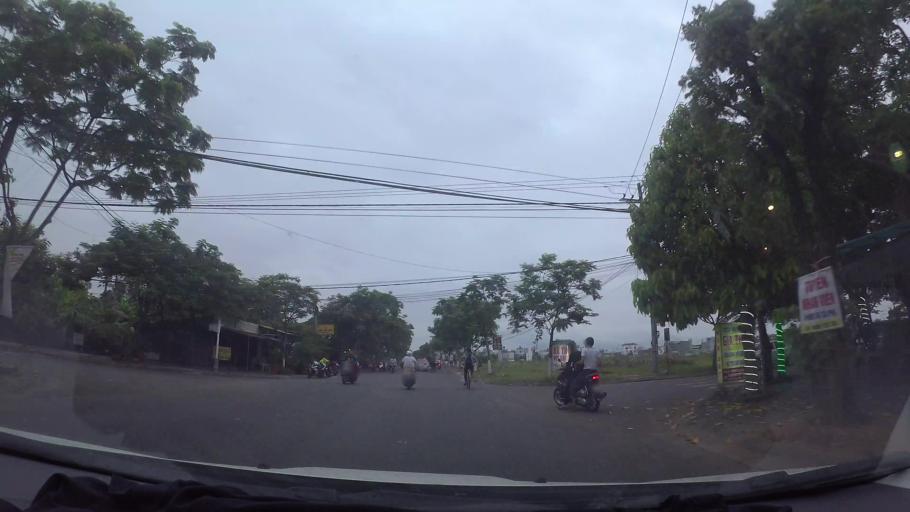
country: VN
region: Da Nang
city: Lien Chieu
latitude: 16.0741
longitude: 108.1578
